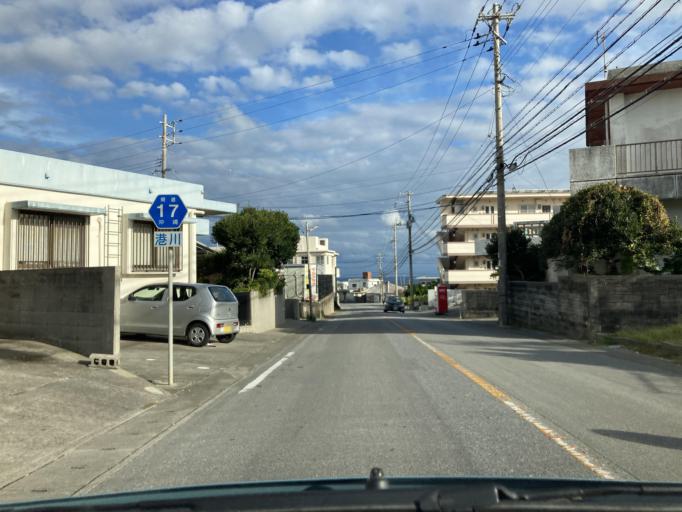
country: JP
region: Okinawa
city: Itoman
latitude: 26.1273
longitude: 127.7568
